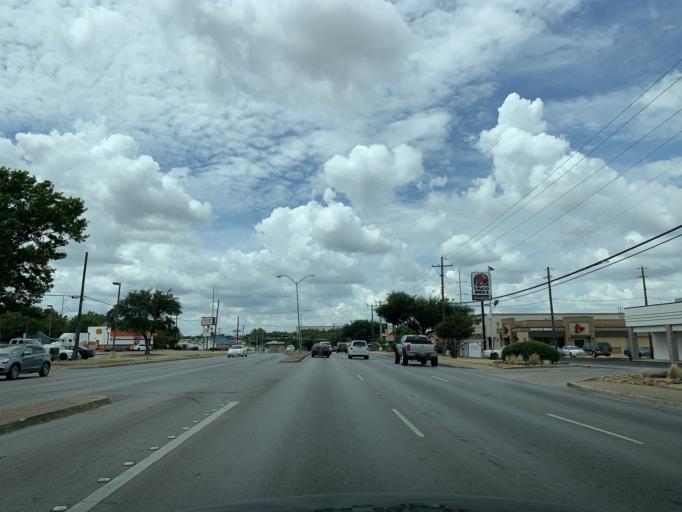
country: US
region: Texas
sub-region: Dallas County
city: Cockrell Hill
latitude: 32.7546
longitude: -96.8721
